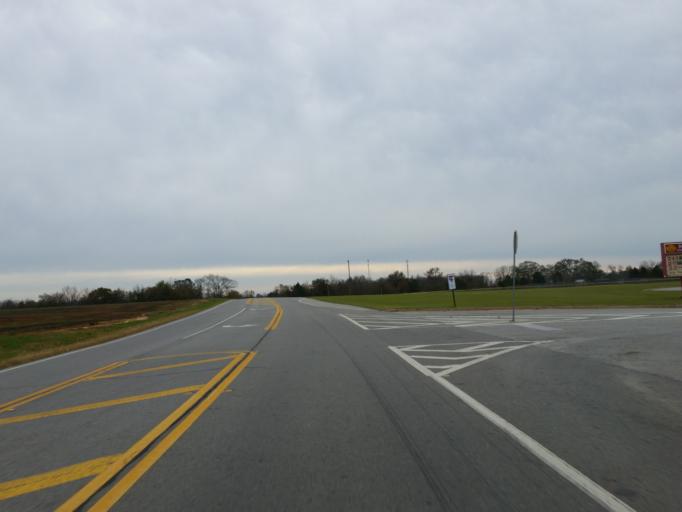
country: US
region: Georgia
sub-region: Dooly County
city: Unadilla
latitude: 32.1850
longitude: -83.7652
